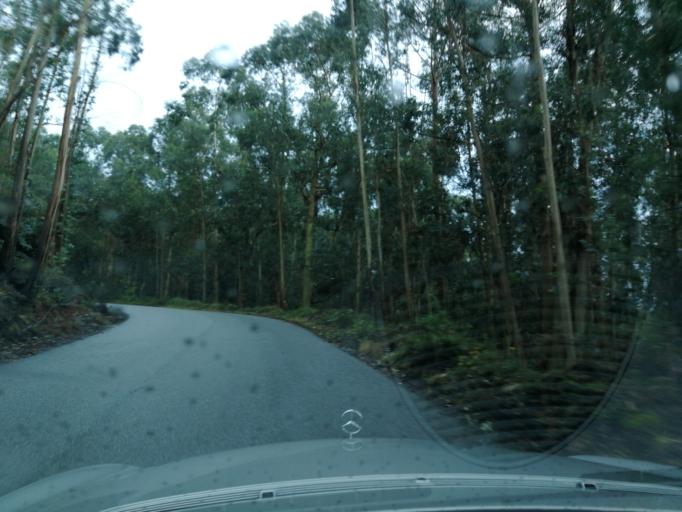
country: PT
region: Braga
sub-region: Braga
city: Oliveira
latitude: 41.4672
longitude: -8.4390
